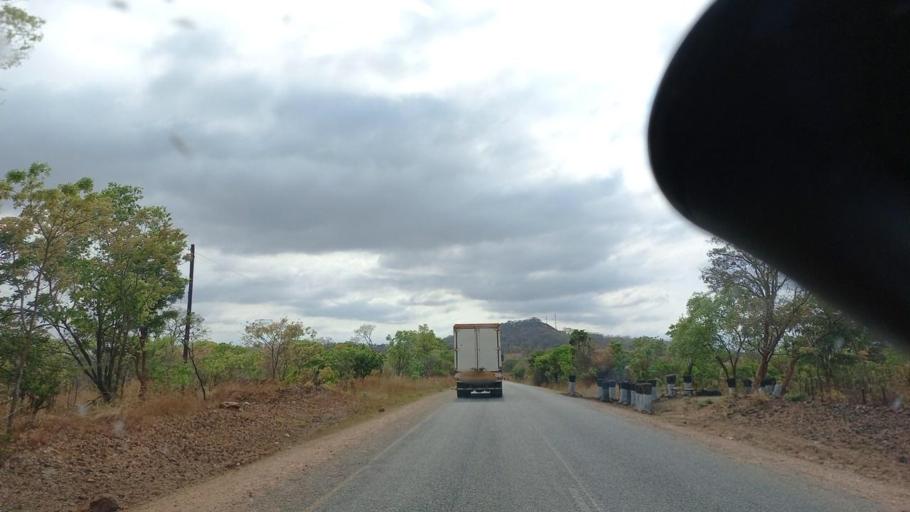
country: ZM
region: Lusaka
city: Chongwe
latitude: -15.1314
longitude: 29.5138
